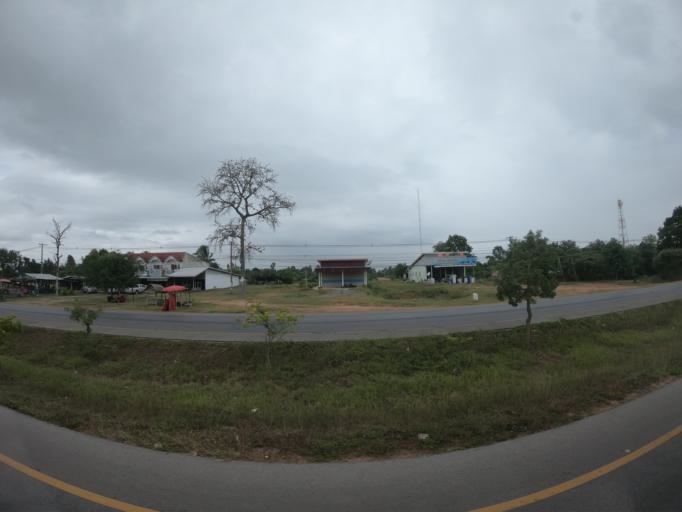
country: TH
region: Maha Sarakham
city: Kut Rang
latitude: 16.0533
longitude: 102.9948
